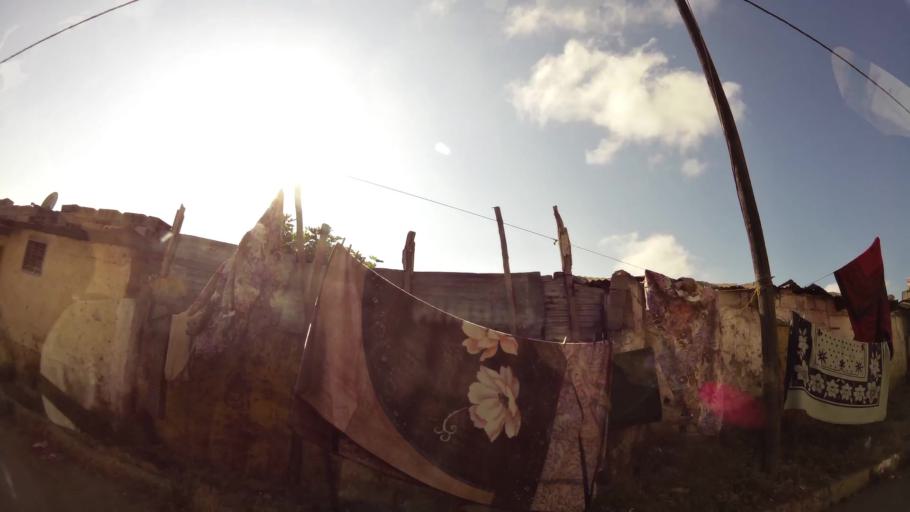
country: MA
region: Rabat-Sale-Zemmour-Zaer
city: Sale
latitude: 34.0481
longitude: -6.8024
